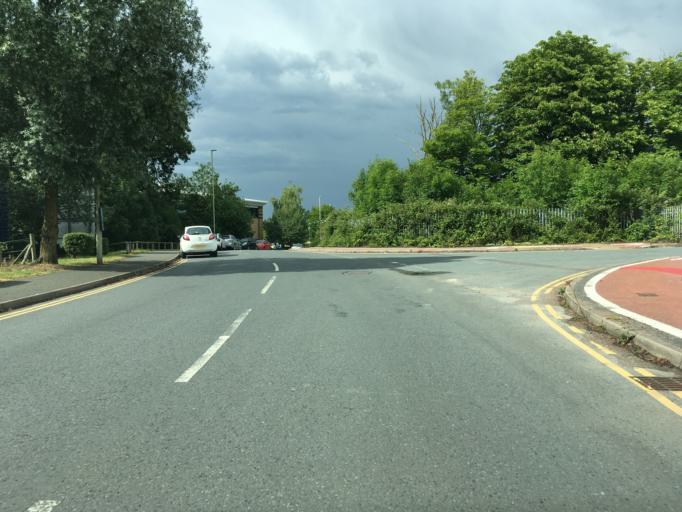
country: GB
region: England
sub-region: Gloucestershire
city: Stonehouse
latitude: 51.8118
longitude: -2.2796
